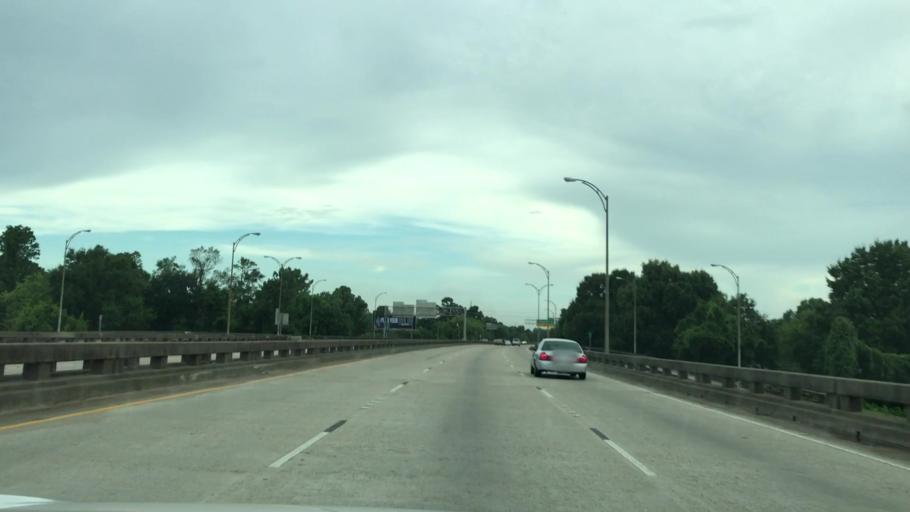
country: US
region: Louisiana
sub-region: East Baton Rouge Parish
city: Baton Rouge
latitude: 30.4986
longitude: -91.1598
